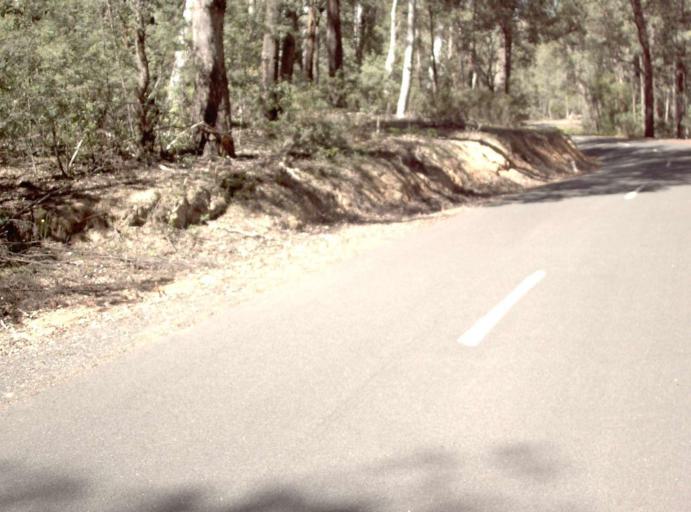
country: AU
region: New South Wales
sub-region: Bombala
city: Bombala
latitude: -37.1128
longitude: 148.7561
